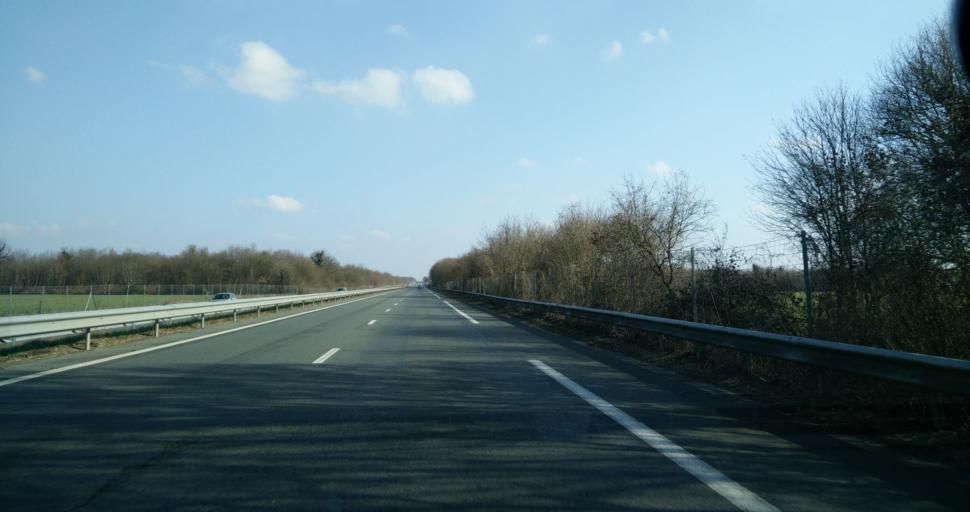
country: FR
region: Poitou-Charentes
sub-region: Departement de la Charente-Maritime
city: Courcon
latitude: 46.2241
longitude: -0.8323
